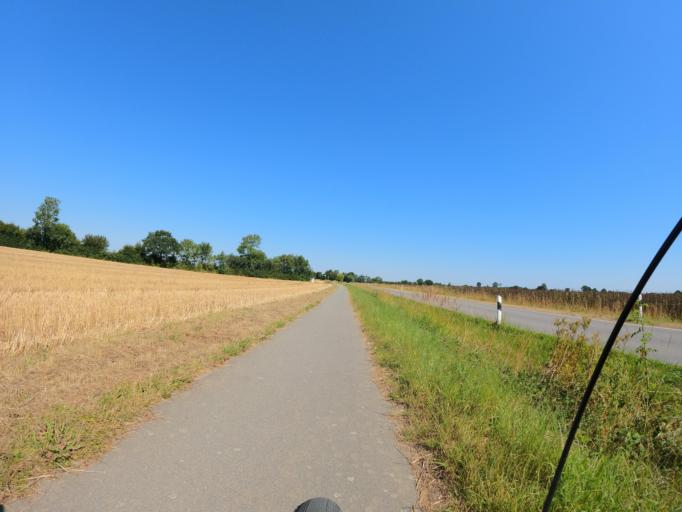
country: DE
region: Schleswig-Holstein
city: Steinbergkirche
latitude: 54.7632
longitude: 9.7638
